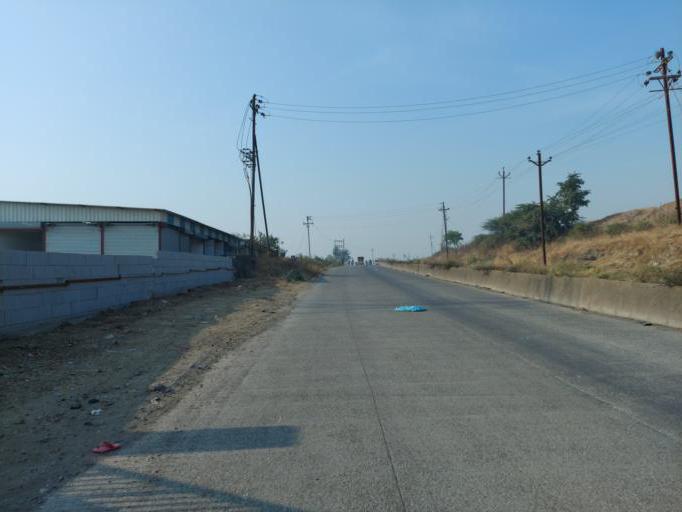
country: IN
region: Maharashtra
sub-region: Pune Division
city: Pune
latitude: 18.4591
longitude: 73.9482
